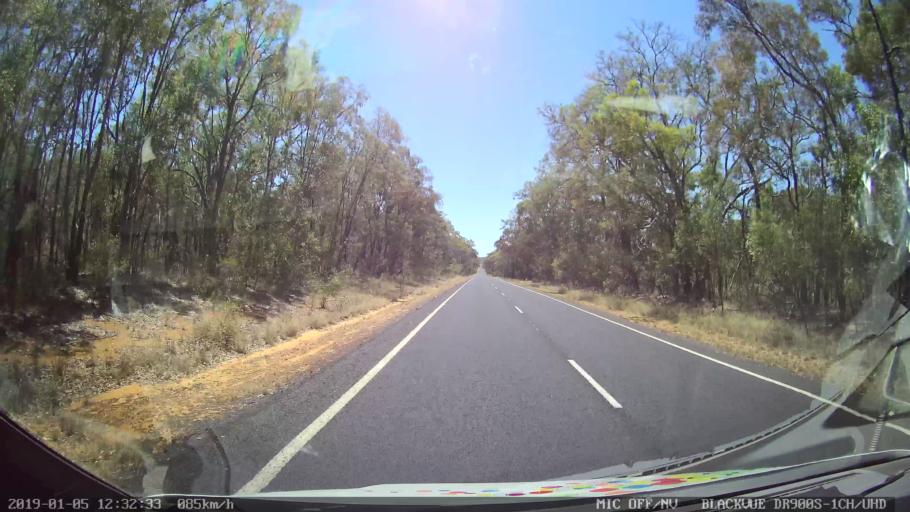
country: AU
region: New South Wales
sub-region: Warrumbungle Shire
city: Coonabarabran
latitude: -31.2170
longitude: 149.3812
